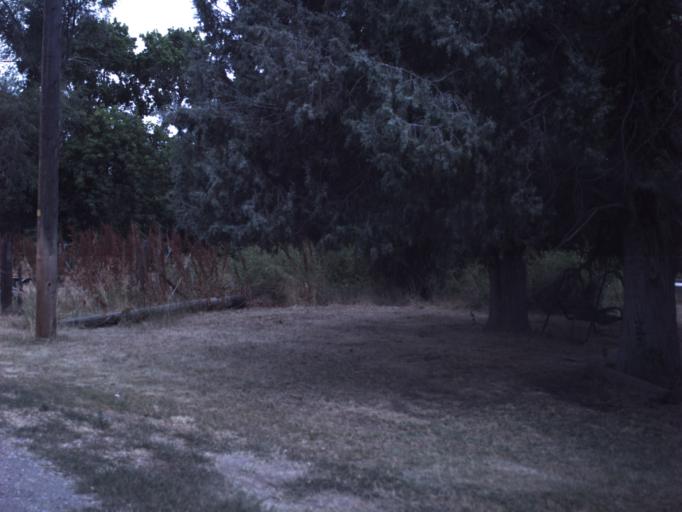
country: US
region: Utah
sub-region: Weber County
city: Washington Terrace
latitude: 41.1455
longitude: -111.9778
